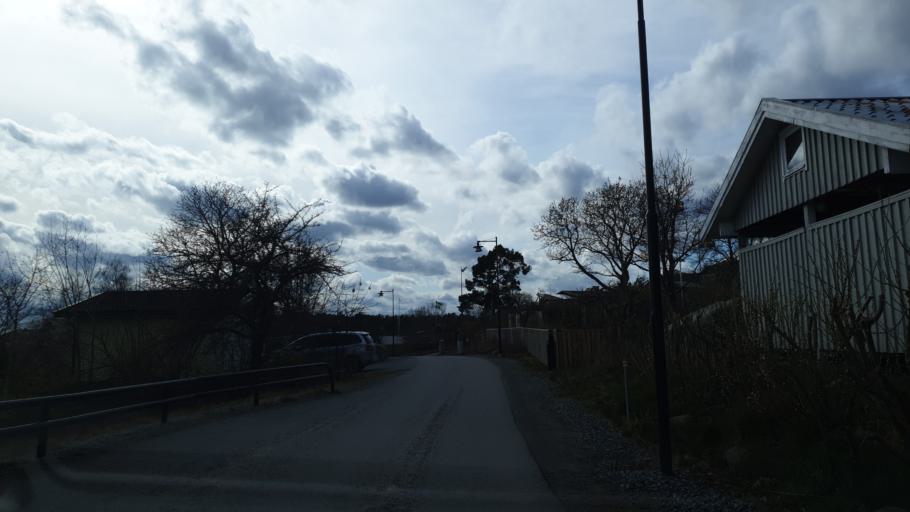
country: SE
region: Stockholm
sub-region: Tyreso Kommun
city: Brevik
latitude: 59.2635
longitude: 18.3539
